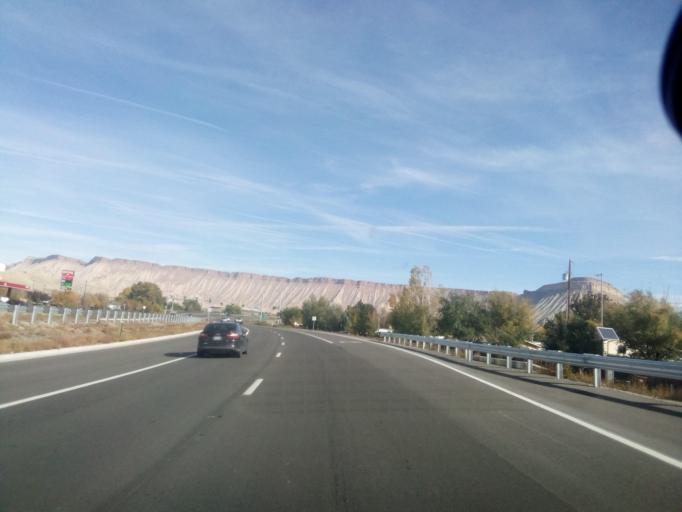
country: US
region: Colorado
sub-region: Mesa County
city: Clifton
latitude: 39.0960
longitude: -108.4494
